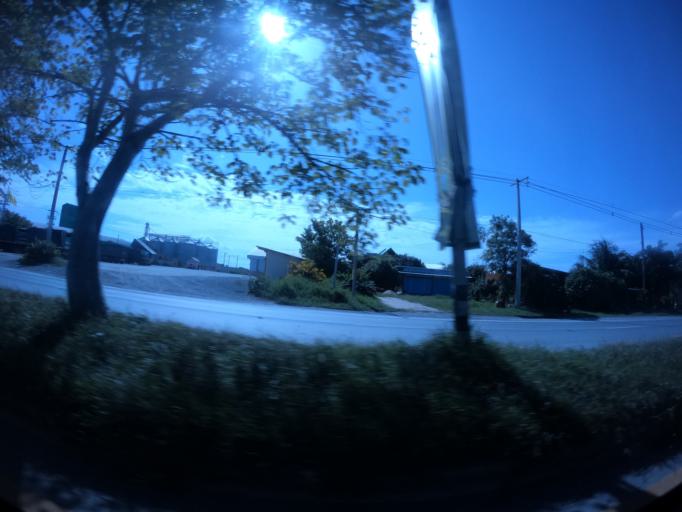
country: TH
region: Nakhon Nayok
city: Ban Na
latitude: 14.2291
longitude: 101.0704
